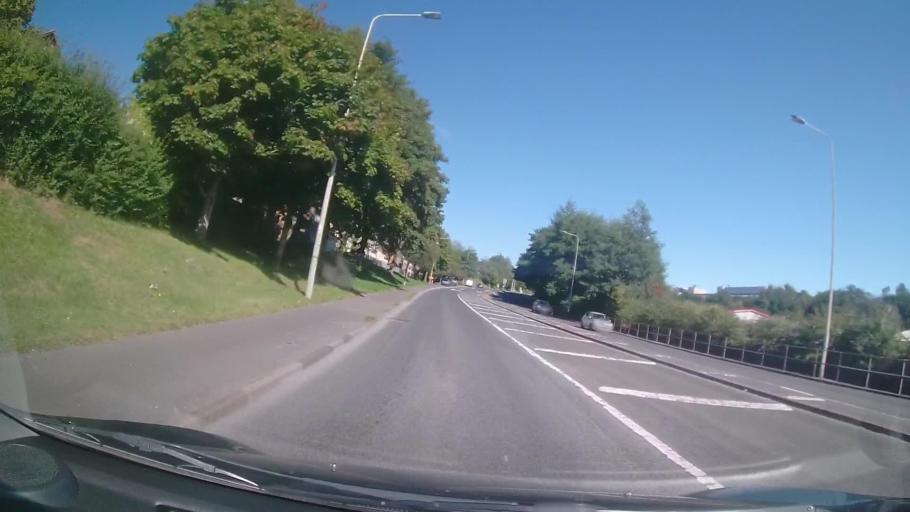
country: GB
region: Wales
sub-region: Merthyr Tydfil County Borough
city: Merthyr Tydfil
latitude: 51.7596
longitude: -3.3552
